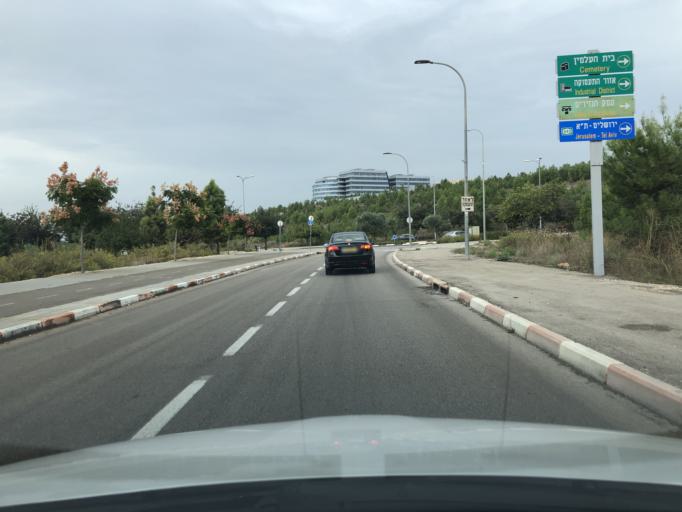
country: PS
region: West Bank
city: Al Midyah
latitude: 31.9201
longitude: 34.9951
